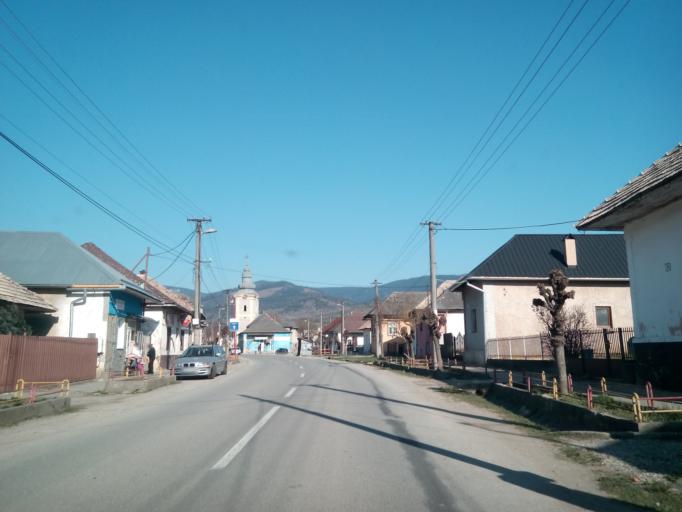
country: SK
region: Kosicky
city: Dobsina
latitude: 48.7115
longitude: 20.2867
